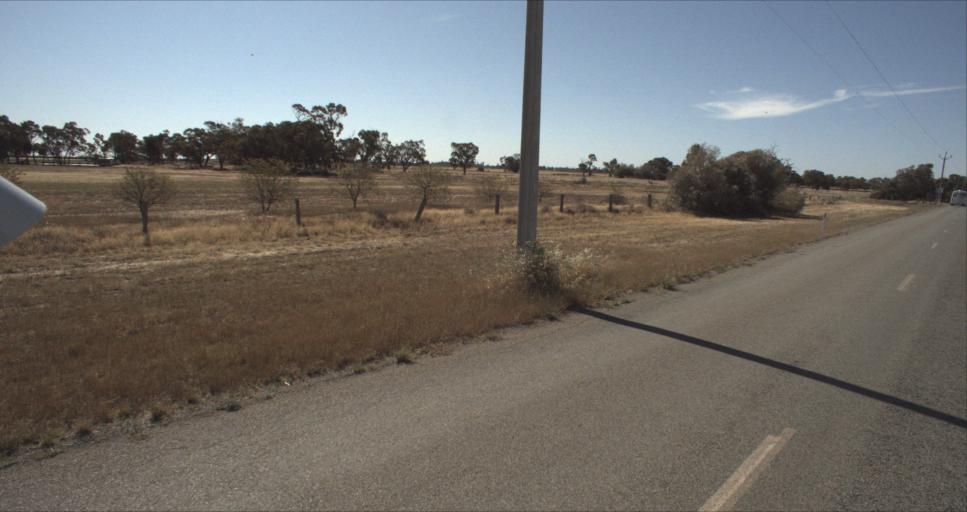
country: AU
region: New South Wales
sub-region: Leeton
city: Leeton
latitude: -34.5708
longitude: 146.3817
